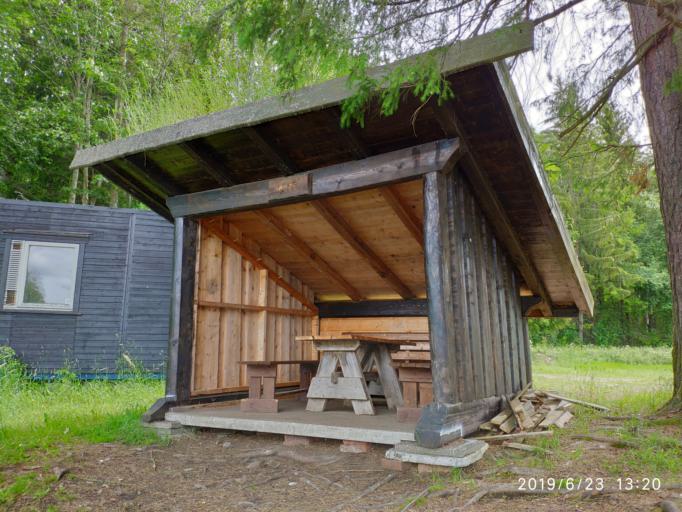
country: NO
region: Buskerud
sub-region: Ringerike
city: Honefoss
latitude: 60.1916
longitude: 10.3089
